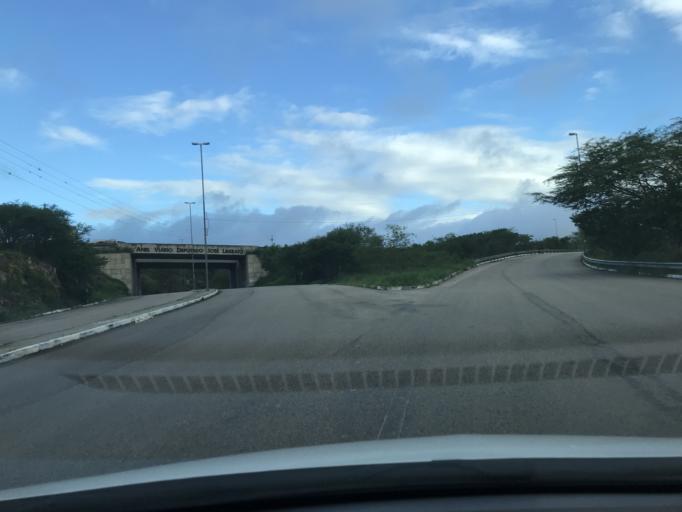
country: BR
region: Pernambuco
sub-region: Caruaru
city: Caruaru
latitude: -8.3063
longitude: -35.9428
